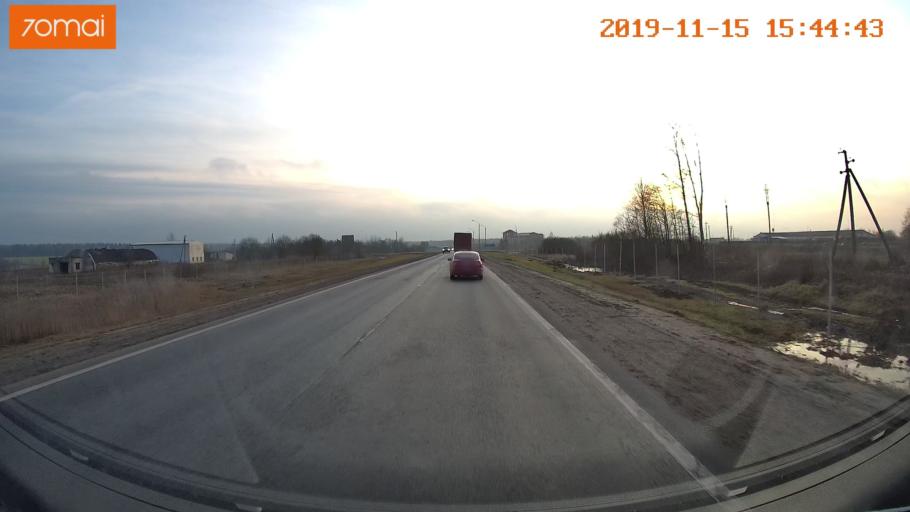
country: RU
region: Jaroslavl
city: Danilov
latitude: 57.9673
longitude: 40.0195
